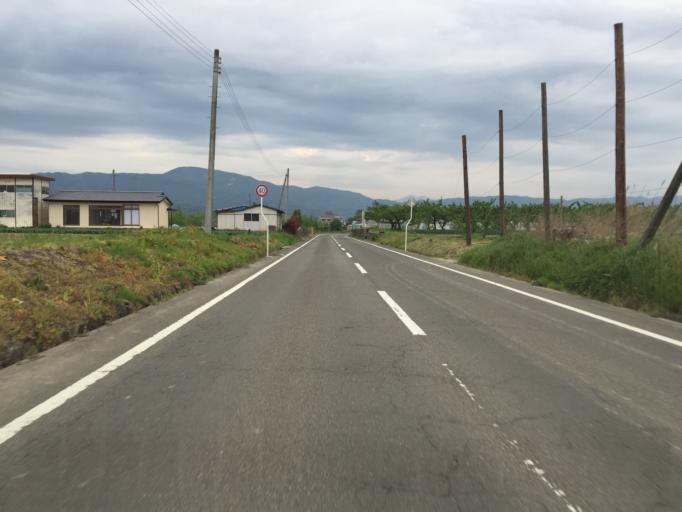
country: JP
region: Fukushima
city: Hobaramachi
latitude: 37.8234
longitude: 140.5366
